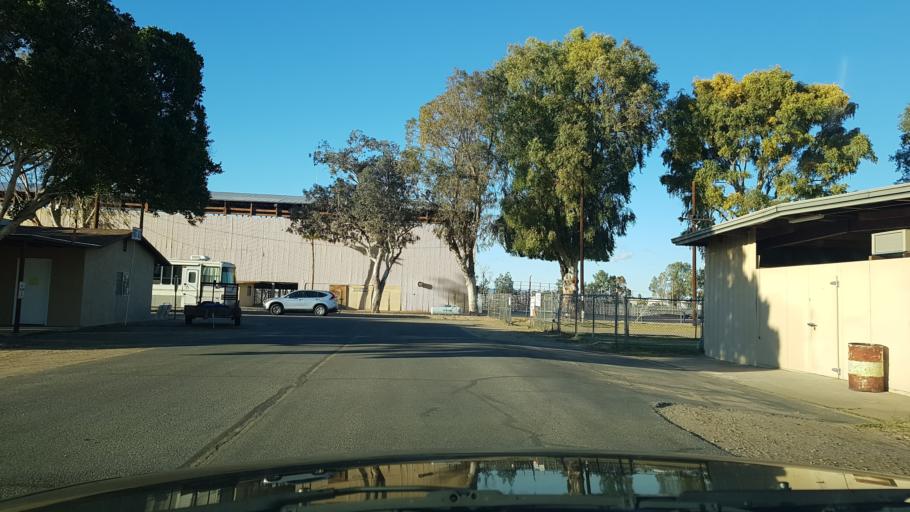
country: US
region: Arizona
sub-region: Yuma County
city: Yuma
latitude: 32.6727
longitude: -114.5928
